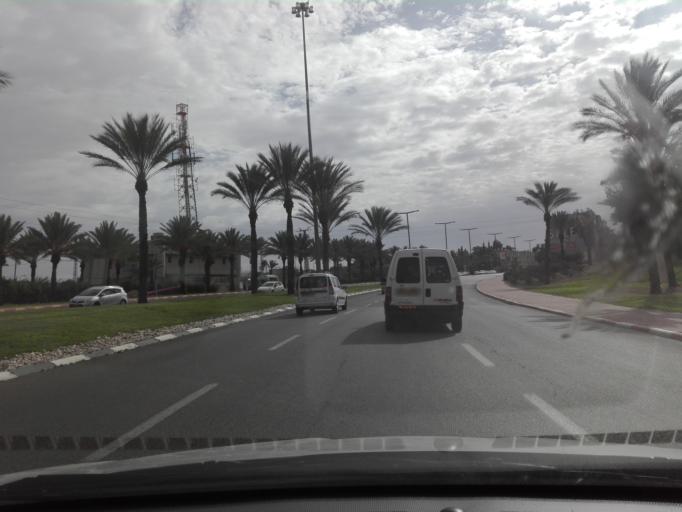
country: IL
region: Southern District
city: Beersheba
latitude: 31.2740
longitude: 34.7971
